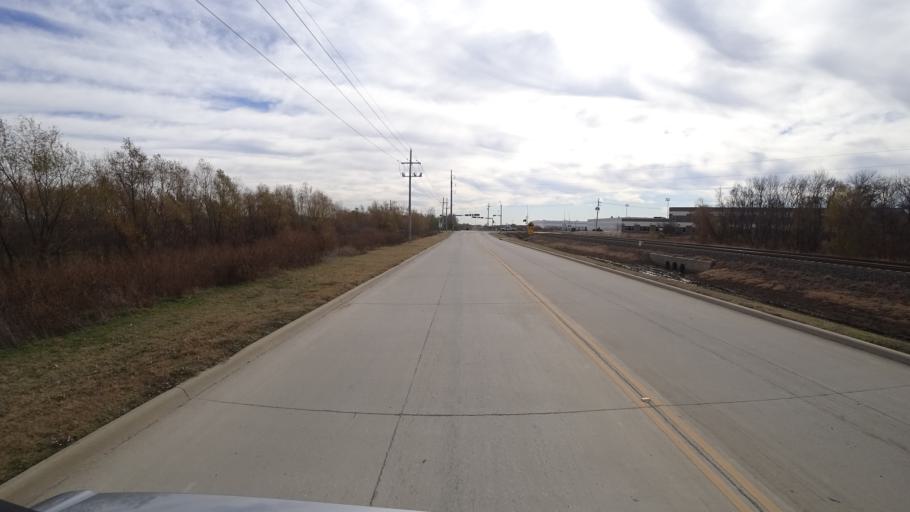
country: US
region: Texas
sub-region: Denton County
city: Lewisville
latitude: 33.0284
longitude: -96.9737
